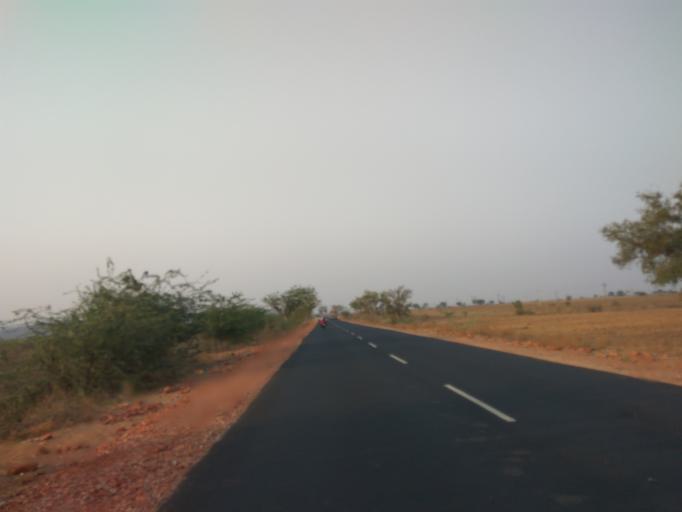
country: IN
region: Andhra Pradesh
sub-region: Prakasam
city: Cumbum
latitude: 15.6202
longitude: 79.1332
